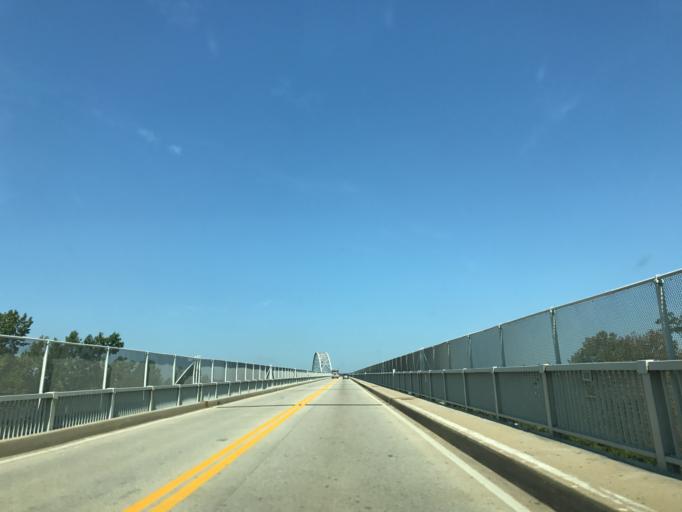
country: US
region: Maryland
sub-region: Cecil County
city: Elkton
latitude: 39.5234
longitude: -75.8166
